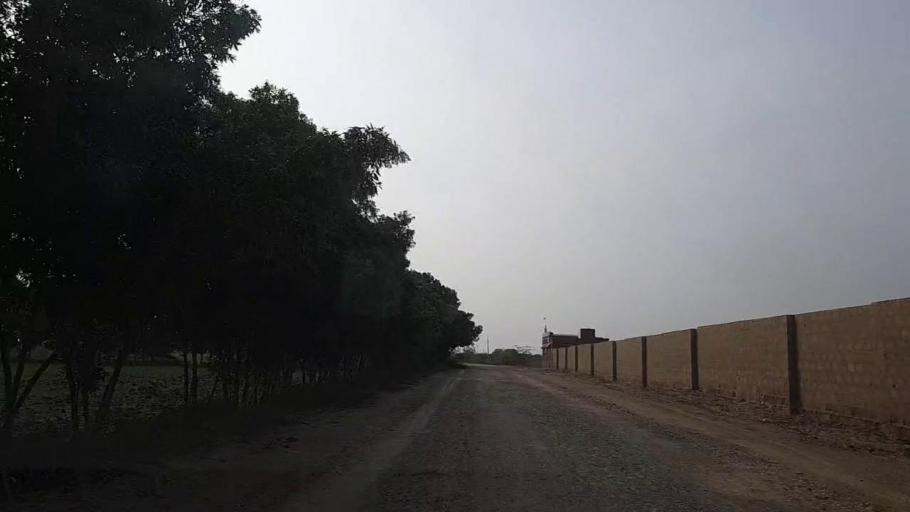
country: PK
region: Sindh
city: Mirpur Sakro
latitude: 24.6446
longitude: 67.6132
